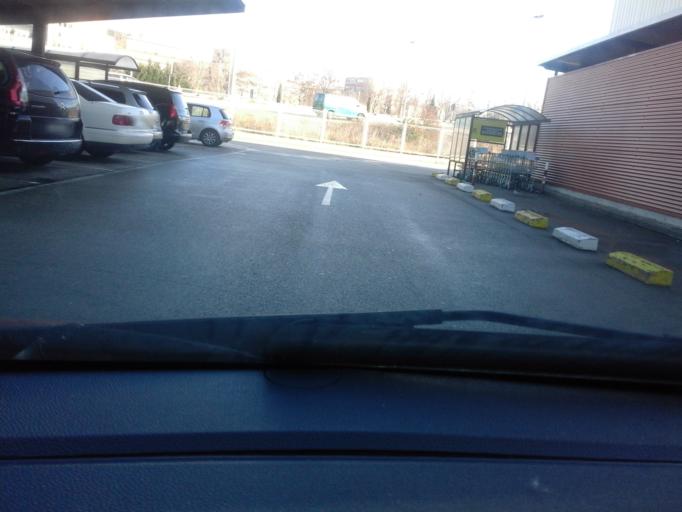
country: ES
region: Navarre
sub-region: Provincia de Navarra
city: Berriozar
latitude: 42.8326
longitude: -1.6748
